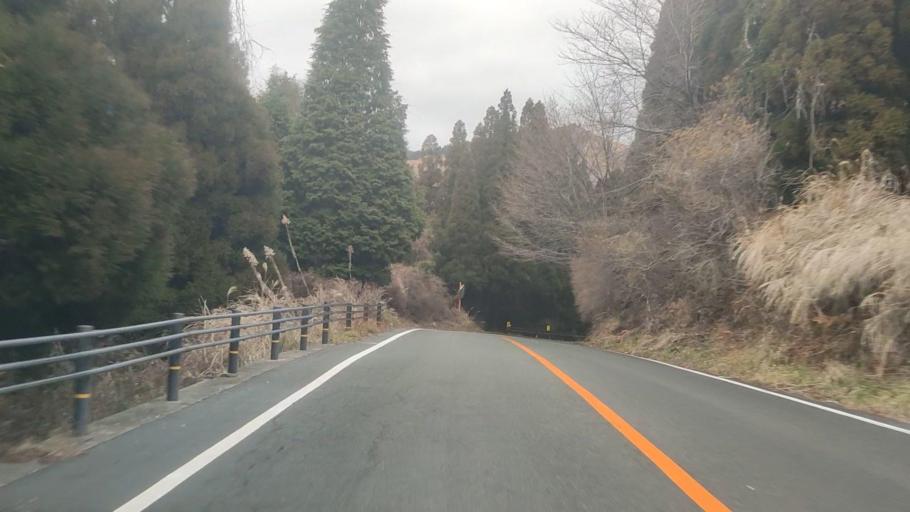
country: JP
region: Kumamoto
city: Aso
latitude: 32.9061
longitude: 131.1444
